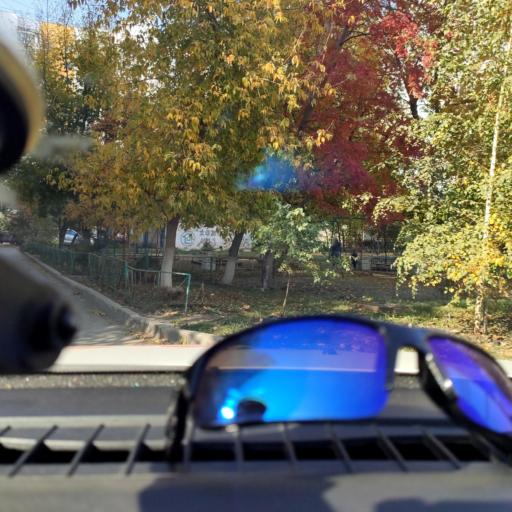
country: RU
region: Samara
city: Samara
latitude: 53.2521
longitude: 50.2109
